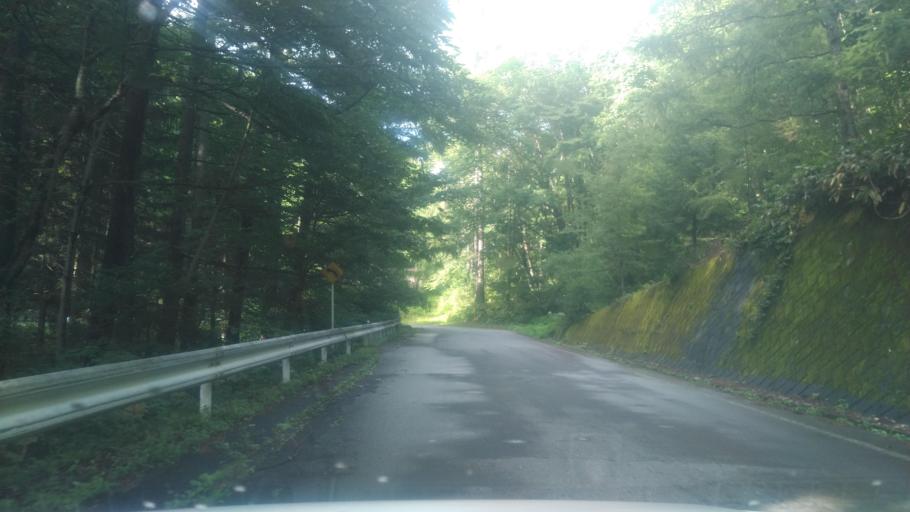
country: JP
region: Nagano
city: Ueda
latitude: 36.5096
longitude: 138.3753
